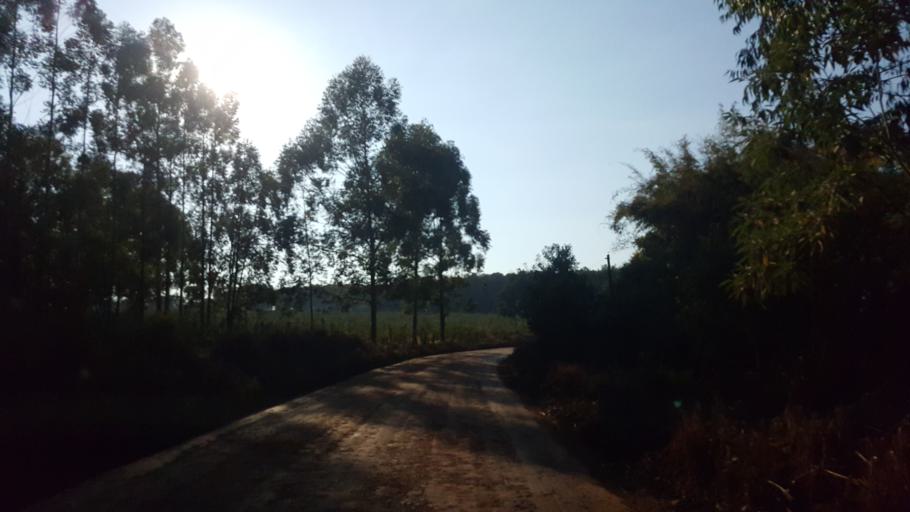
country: AR
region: Misiones
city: Capiovi
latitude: -26.8905
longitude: -55.0658
